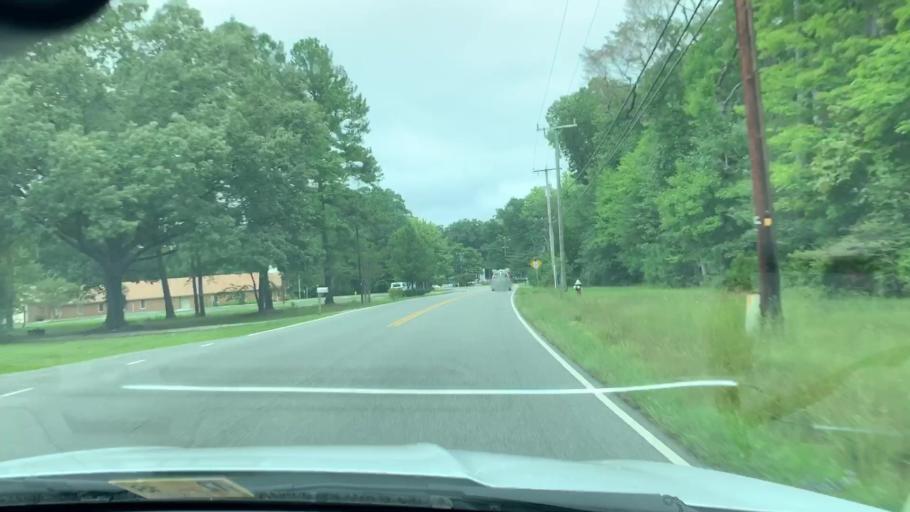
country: US
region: Virginia
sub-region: York County
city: Yorktown
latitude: 37.1898
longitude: -76.4362
